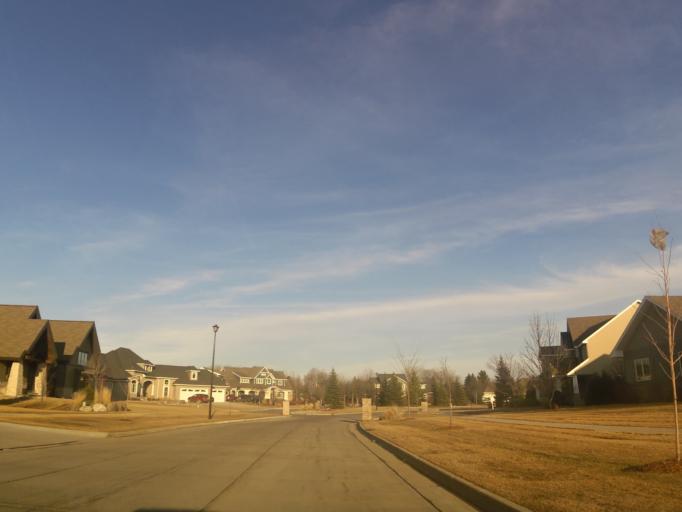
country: US
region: North Dakota
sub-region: Grand Forks County
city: Grand Forks
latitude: 47.8698
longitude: -97.0347
